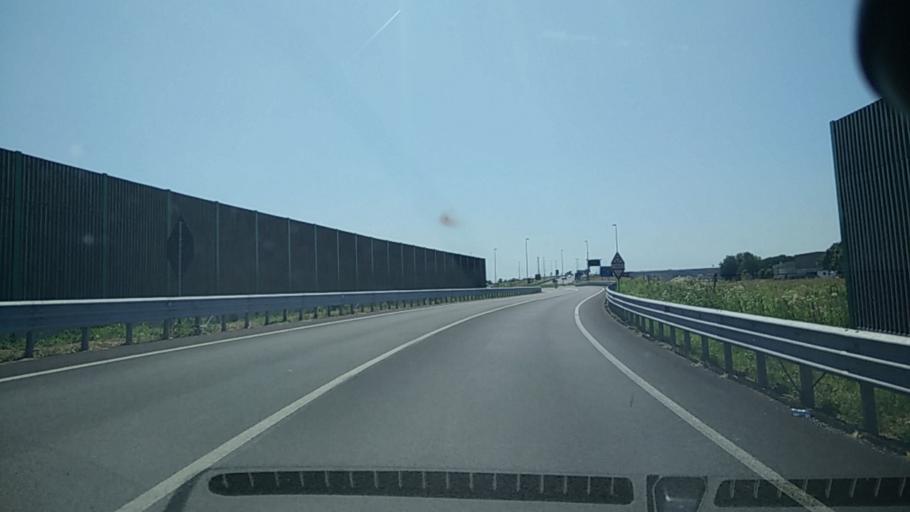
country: IT
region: Veneto
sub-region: Provincia di Venezia
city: Marcon-Gaggio-Colmello
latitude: 45.5505
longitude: 12.2945
